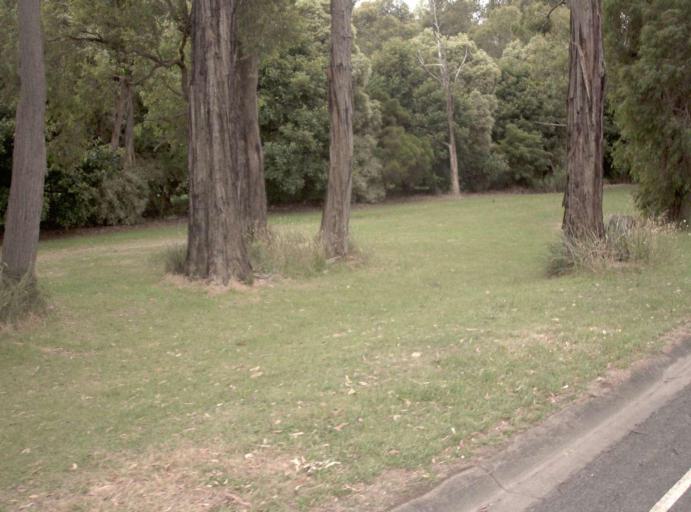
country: AU
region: Victoria
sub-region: Yarra Ranges
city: Mount Evelyn
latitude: -37.7651
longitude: 145.4021
